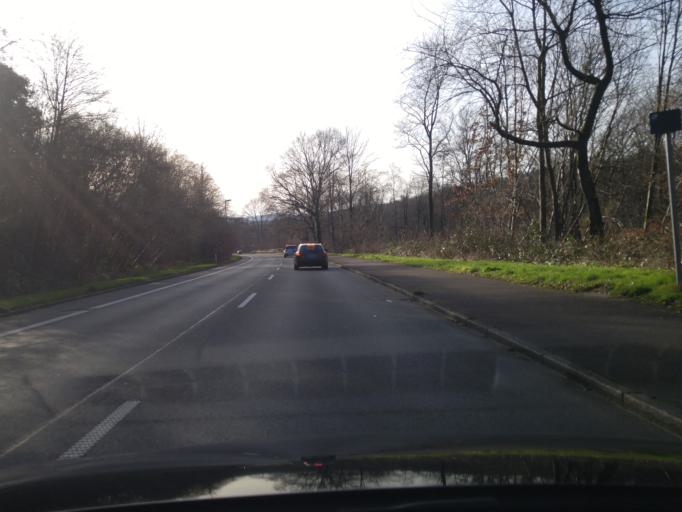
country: DE
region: North Rhine-Westphalia
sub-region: Regierungsbezirk Dusseldorf
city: Essen
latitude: 51.4135
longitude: 7.0191
